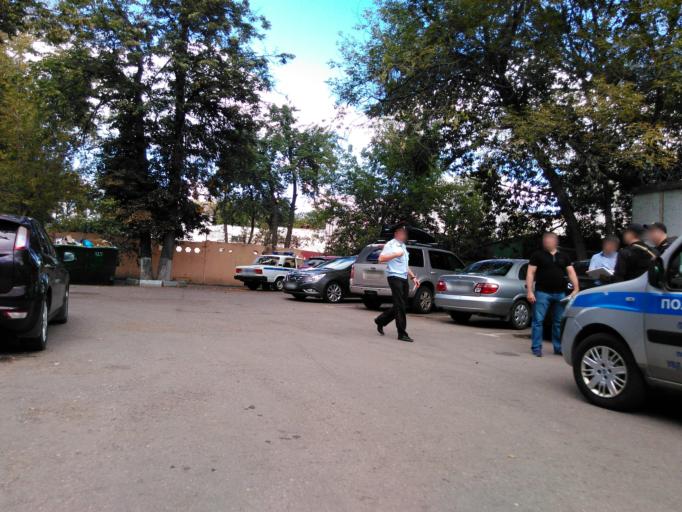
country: RU
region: Moscow
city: Novyye Cheremushki
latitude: 55.6916
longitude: 37.6144
